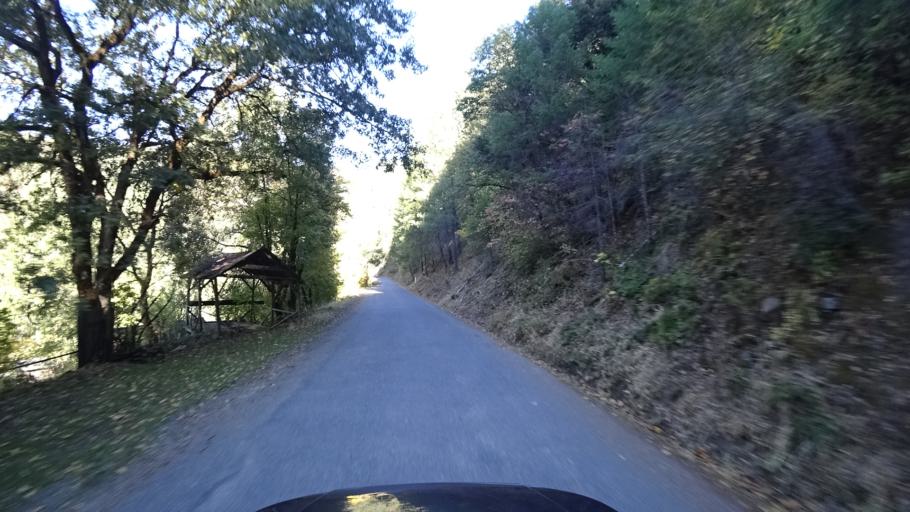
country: US
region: California
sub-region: Humboldt County
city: Willow Creek
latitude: 41.2511
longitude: -123.3125
